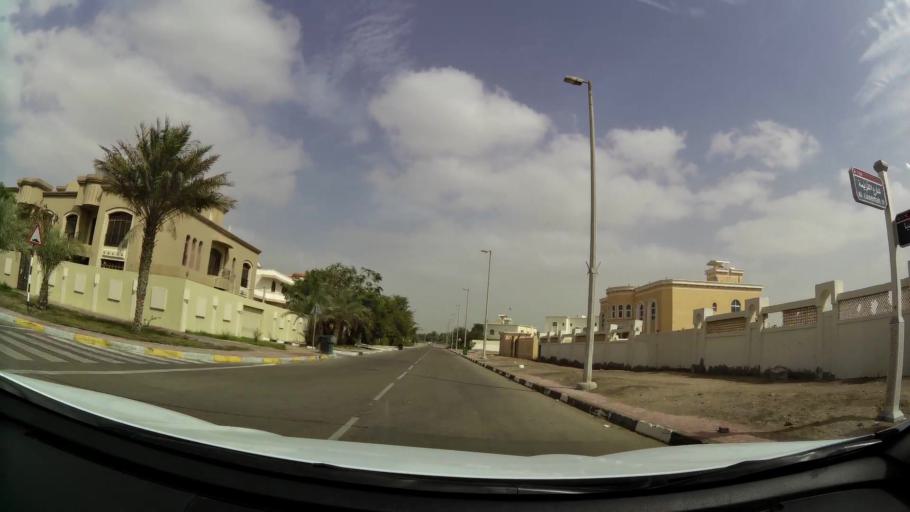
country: AE
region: Abu Dhabi
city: Abu Dhabi
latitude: 24.4016
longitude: 54.5207
